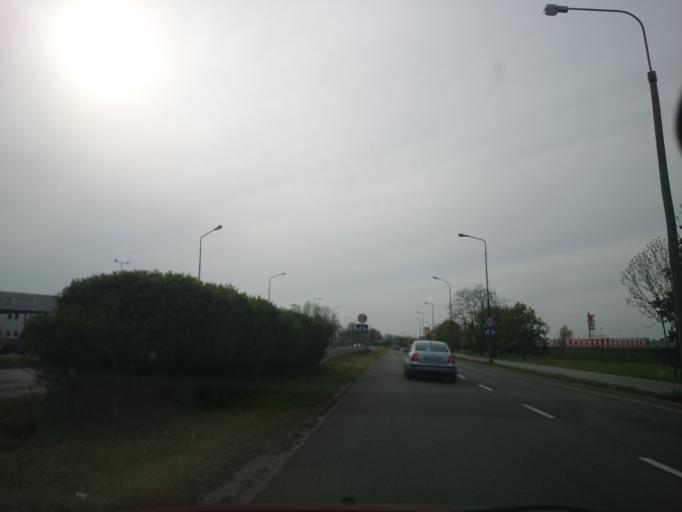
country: PL
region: Opole Voivodeship
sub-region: Powiat opolski
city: Chmielowice
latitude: 50.6785
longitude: 17.8841
